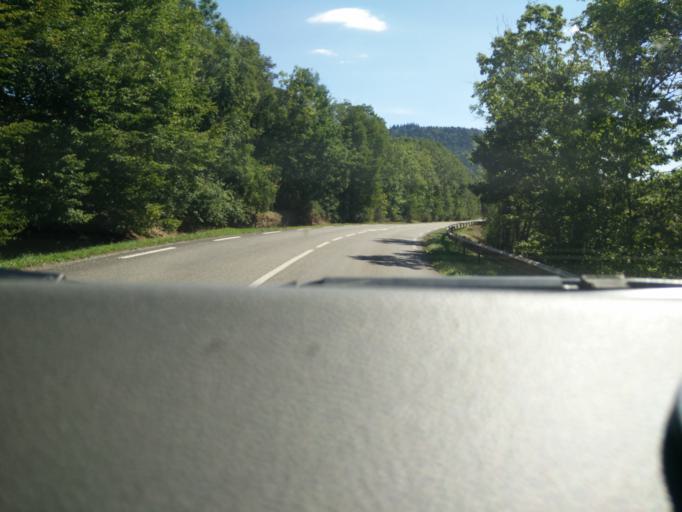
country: FR
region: Lorraine
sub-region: Departement des Vosges
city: Etival-Clairefontaine
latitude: 48.4007
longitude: 6.8514
